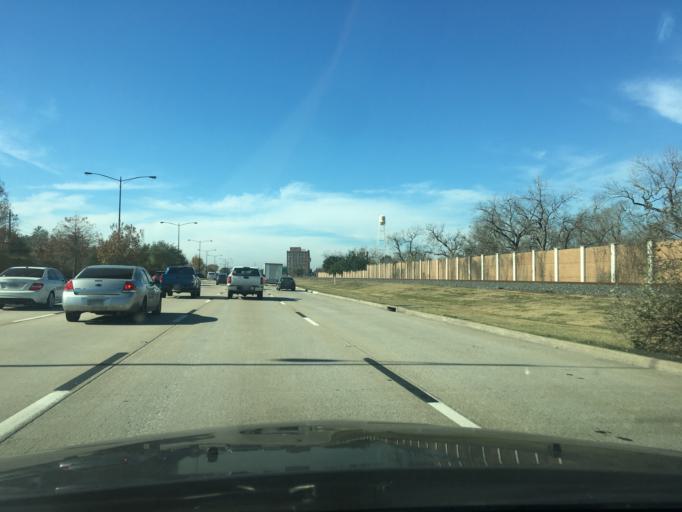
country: US
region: Texas
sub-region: Fort Bend County
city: Sugar Land
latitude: 29.6219
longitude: -95.6259
